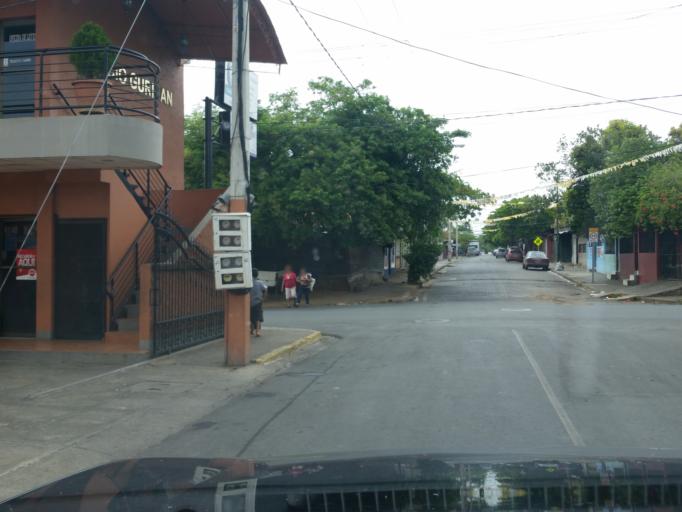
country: NI
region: Managua
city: Managua
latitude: 12.1408
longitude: -86.2533
